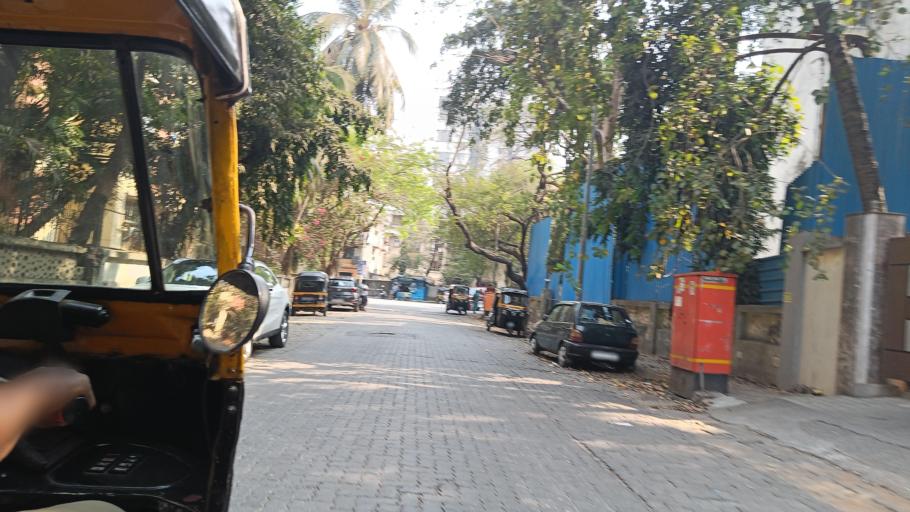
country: IN
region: Maharashtra
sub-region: Mumbai Suburban
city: Mumbai
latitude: 19.1153
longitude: 72.8317
